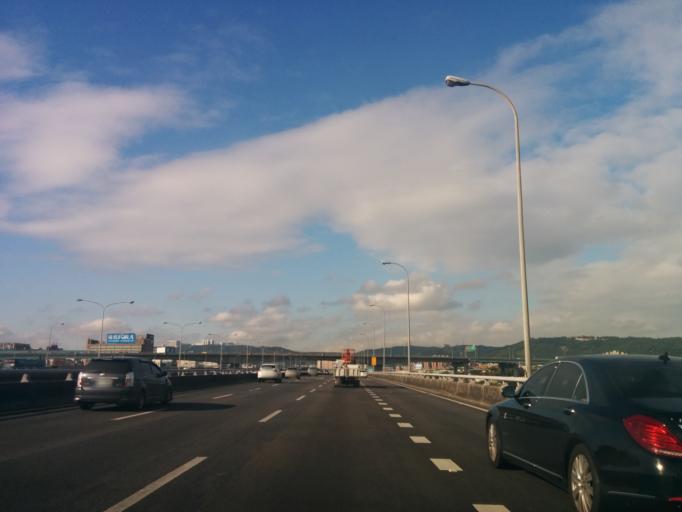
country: TW
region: Taipei
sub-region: Taipei
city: Banqiao
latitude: 25.0751
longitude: 121.4585
